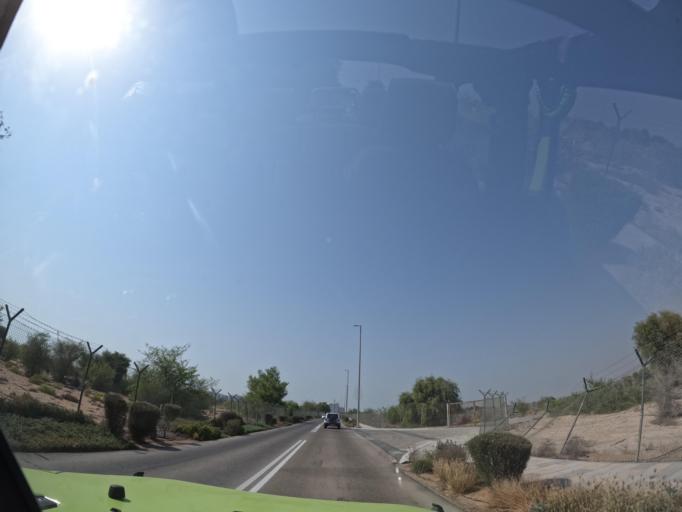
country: AE
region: Abu Dhabi
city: Abu Dhabi
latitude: 24.4749
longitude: 54.6285
